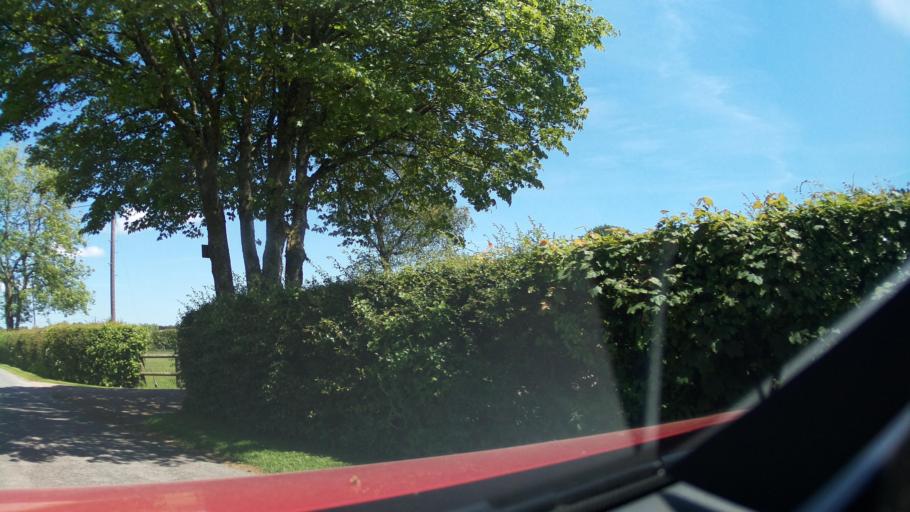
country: GB
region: Wales
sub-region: Monmouthshire
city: Llangwm
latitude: 51.6779
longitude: -2.7676
